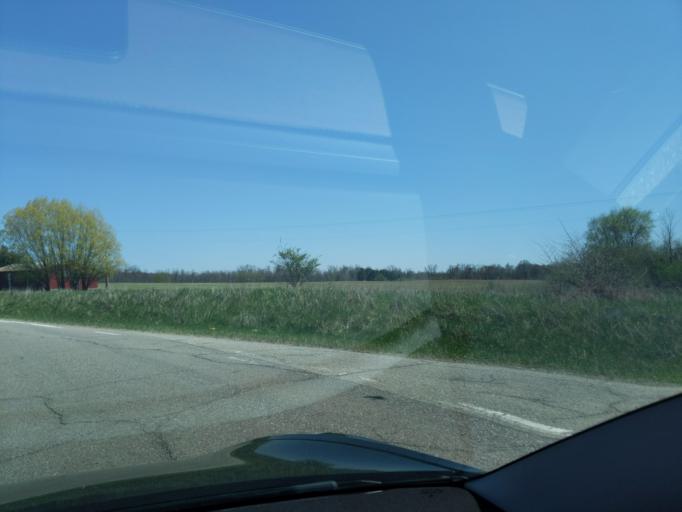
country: US
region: Michigan
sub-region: Ingham County
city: Stockbridge
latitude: 42.5028
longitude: -84.2539
